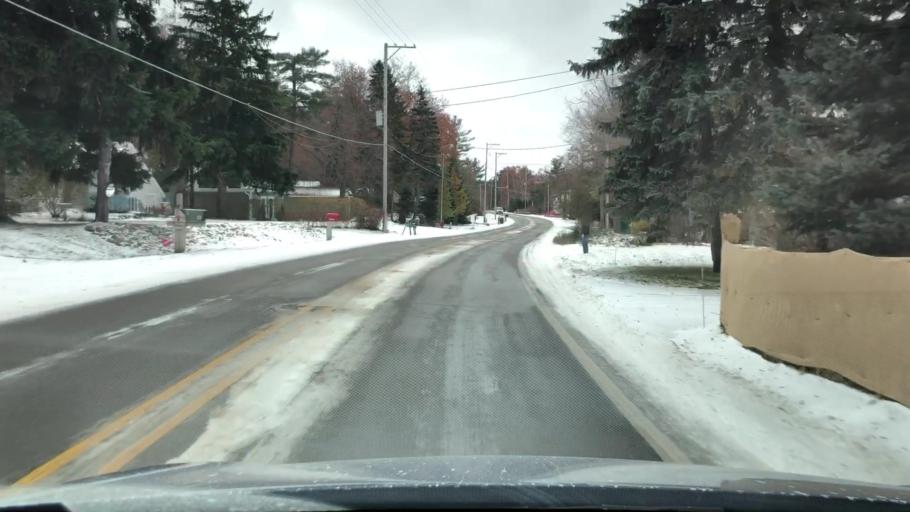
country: US
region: Michigan
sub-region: Grand Traverse County
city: Traverse City
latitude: 44.7838
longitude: -85.5890
